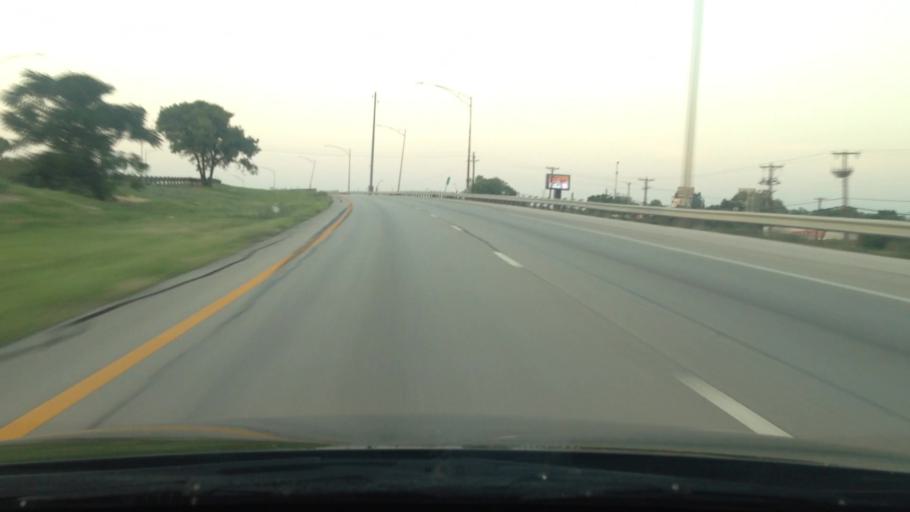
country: US
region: Texas
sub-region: Tarrant County
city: Forest Hill
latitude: 32.7185
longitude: -97.2256
